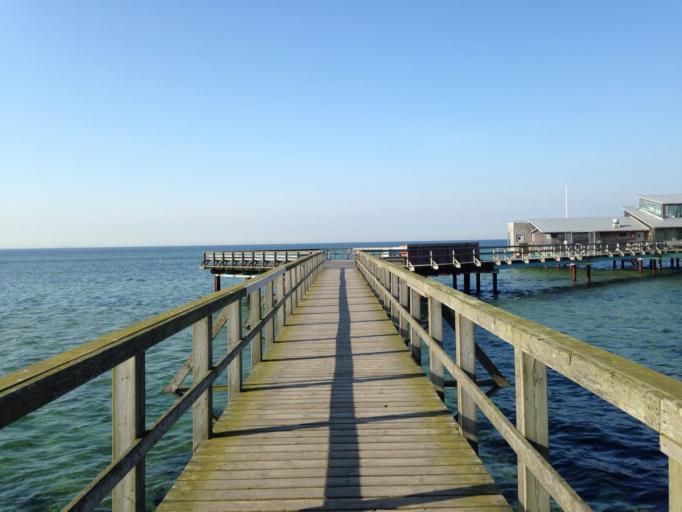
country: SE
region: Skane
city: Bjarred
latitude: 55.7087
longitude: 13.0200
